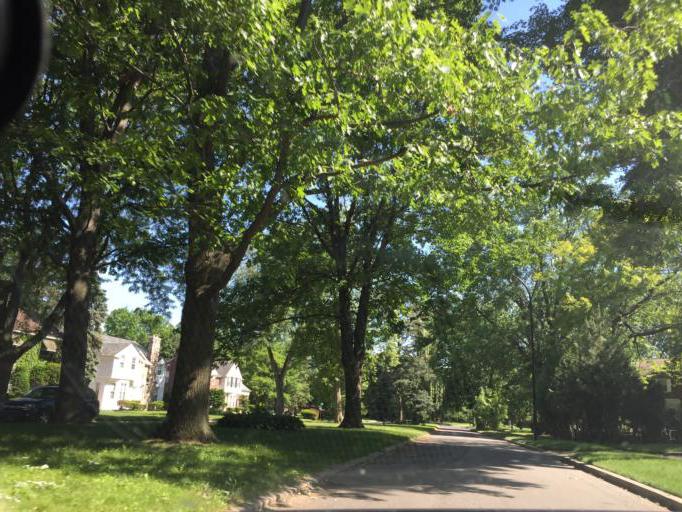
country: US
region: Michigan
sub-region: Oakland County
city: Southfield
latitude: 42.4091
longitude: -83.2289
